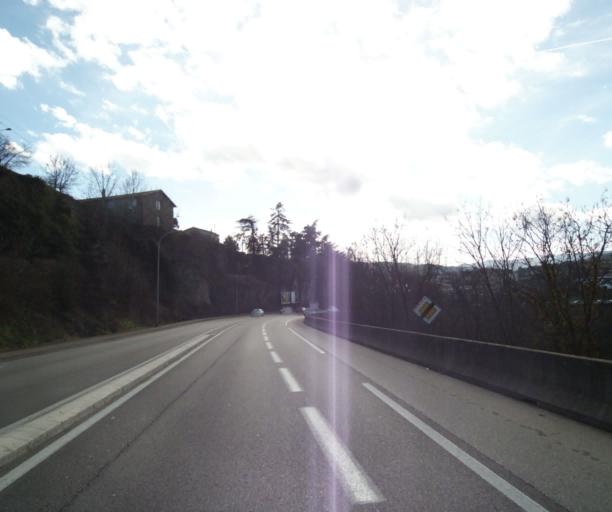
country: FR
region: Rhone-Alpes
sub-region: Departement de l'Ardeche
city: Annonay
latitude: 45.2484
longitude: 4.6794
